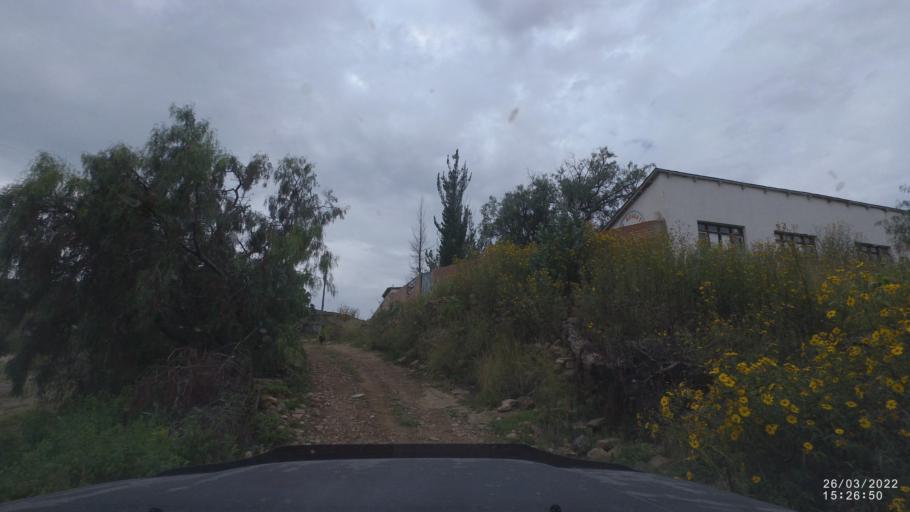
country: BO
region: Cochabamba
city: Cliza
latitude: -17.7509
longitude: -65.8601
